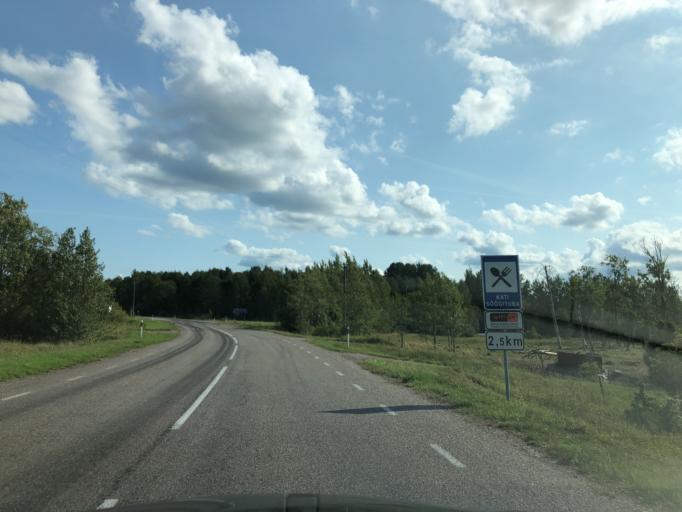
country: EE
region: Hiiumaa
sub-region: Kaerdla linn
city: Kardla
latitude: 58.7205
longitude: 22.5634
